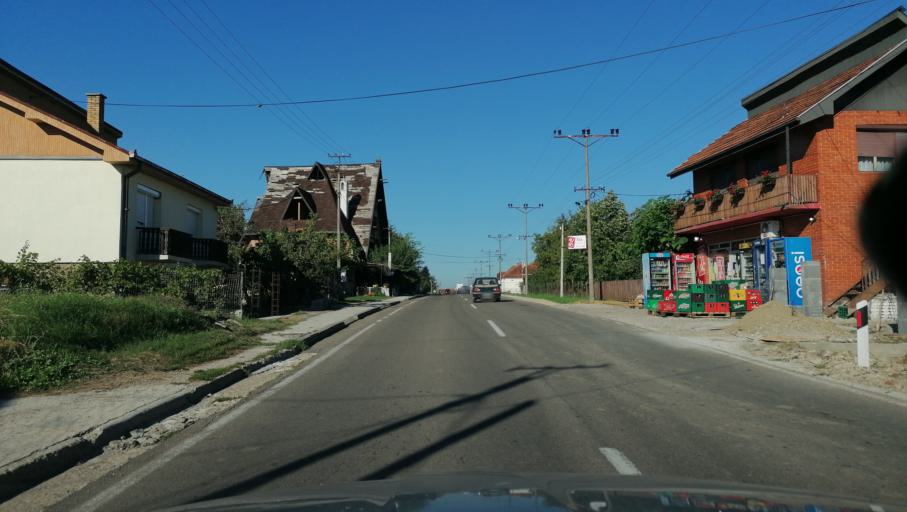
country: RS
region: Central Serbia
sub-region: Sumadijski Okrug
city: Knic
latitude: 43.9010
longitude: 20.6265
